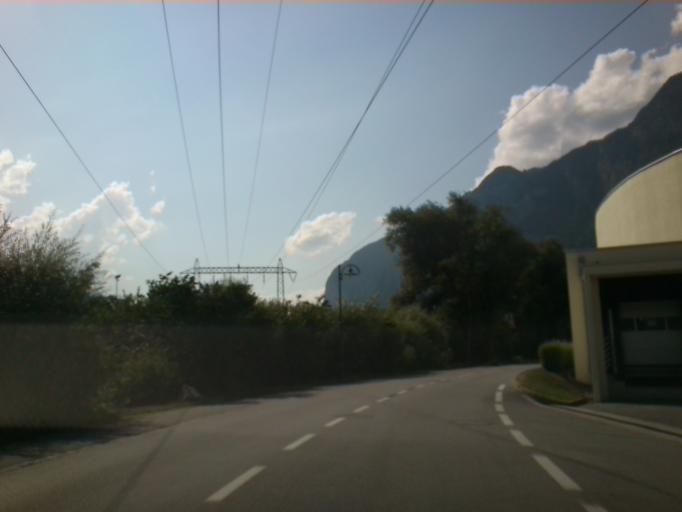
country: AT
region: Tyrol
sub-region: Politischer Bezirk Innsbruck Land
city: Vols
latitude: 47.2556
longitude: 11.3254
